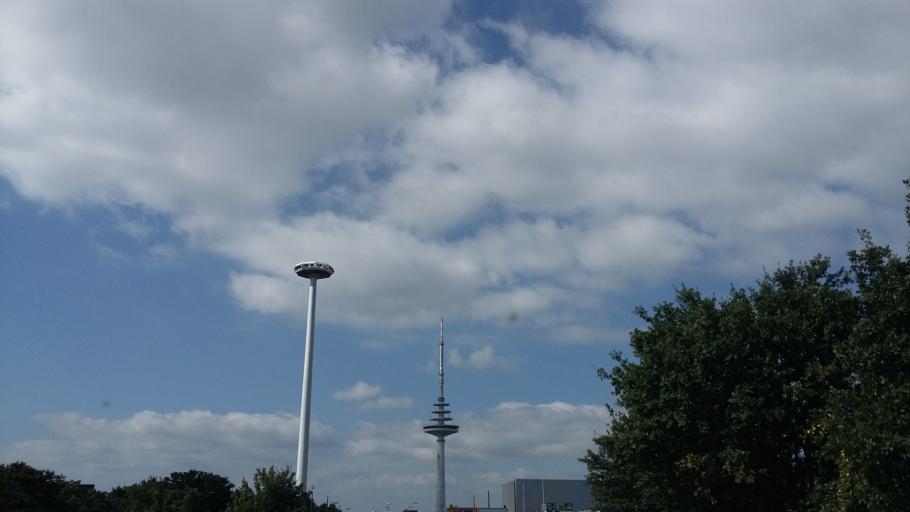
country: DE
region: Bremen
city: Bremen
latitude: 53.0880
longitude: 8.7974
